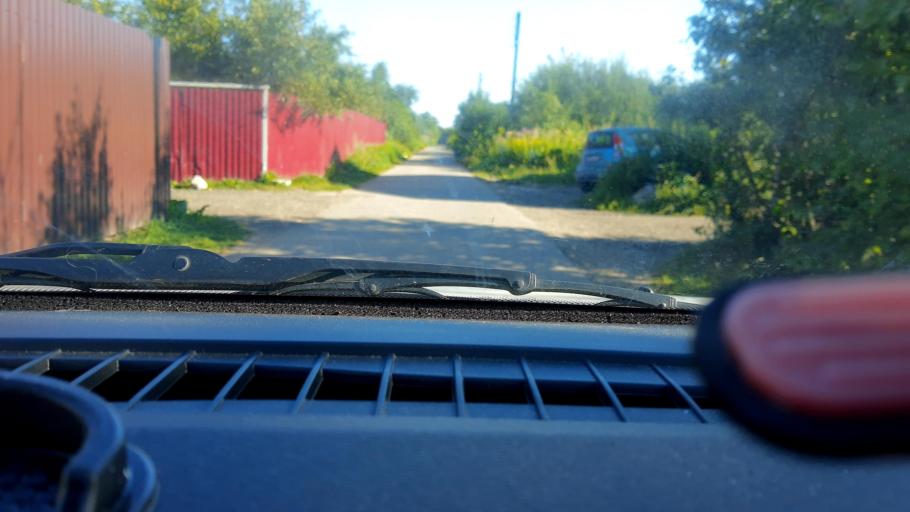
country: RU
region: Nizjnij Novgorod
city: Gorbatovka
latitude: 56.2553
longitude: 43.8141
